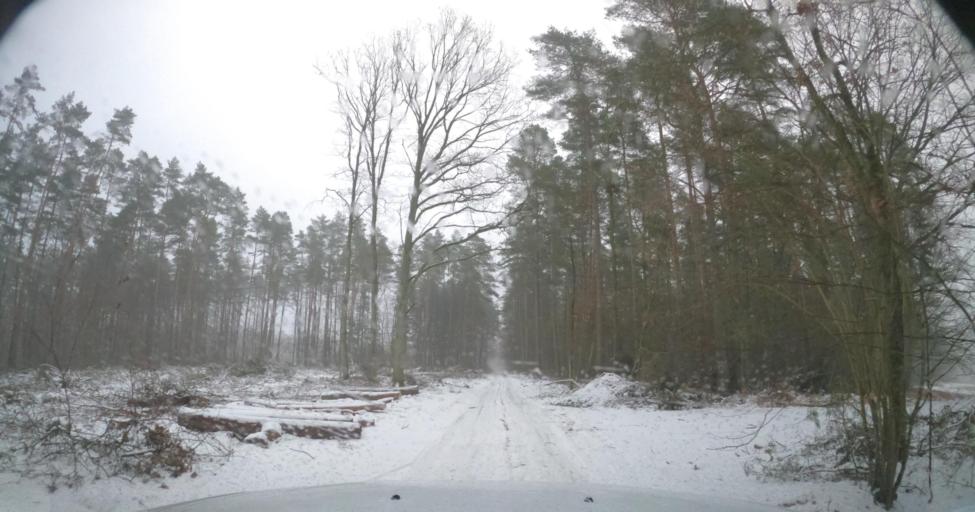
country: PL
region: West Pomeranian Voivodeship
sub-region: Powiat kamienski
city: Golczewo
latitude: 53.7706
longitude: 14.9342
